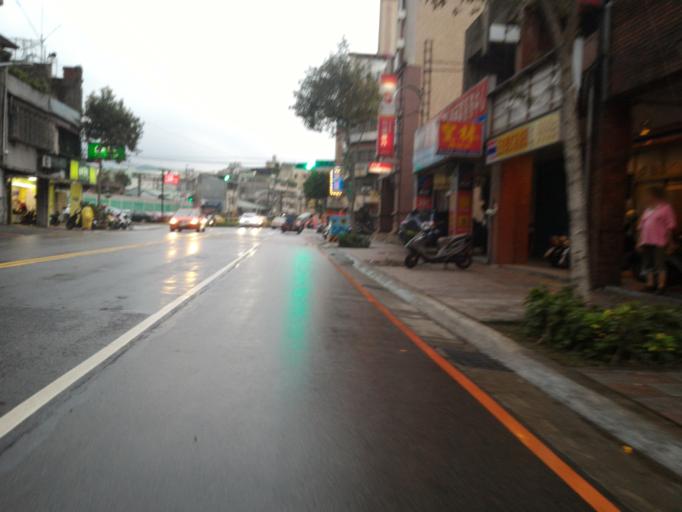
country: TW
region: Taipei
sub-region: Taipei
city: Banqiao
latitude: 24.9874
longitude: 121.4210
